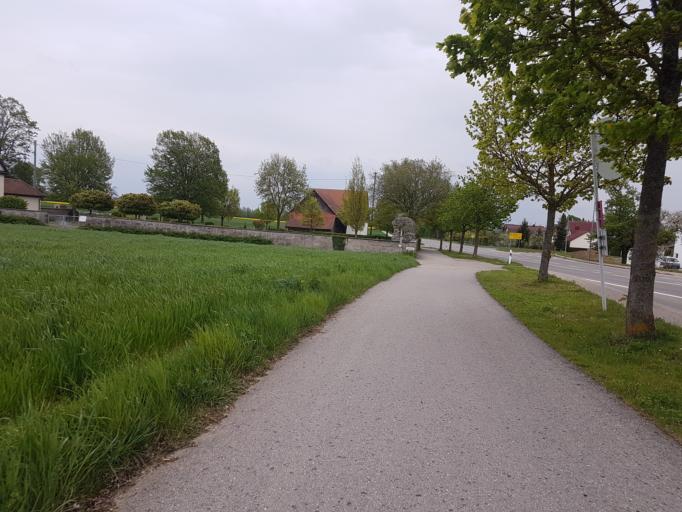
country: DE
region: Baden-Wuerttemberg
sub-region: Regierungsbezirk Stuttgart
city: Motzingen
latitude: 48.4704
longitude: 8.7805
